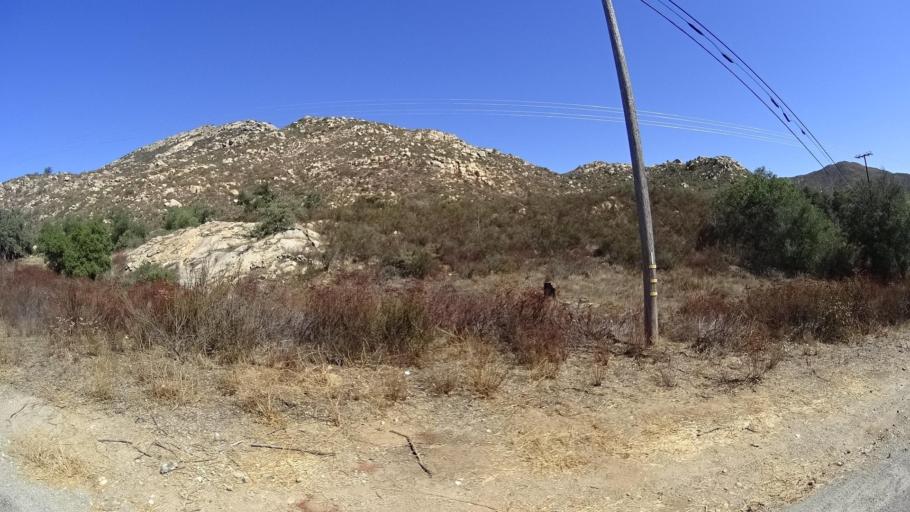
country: US
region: California
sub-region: San Diego County
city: Alpine
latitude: 32.7114
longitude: -116.7438
